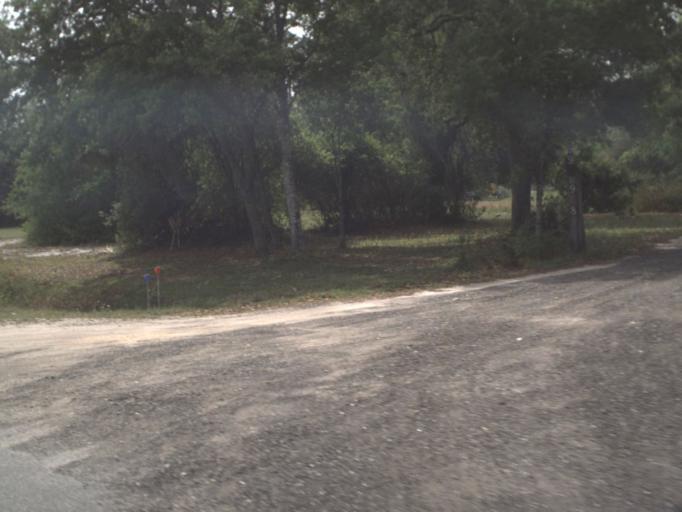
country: US
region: Florida
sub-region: Flagler County
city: Bunnell
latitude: 29.4678
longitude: -81.2751
